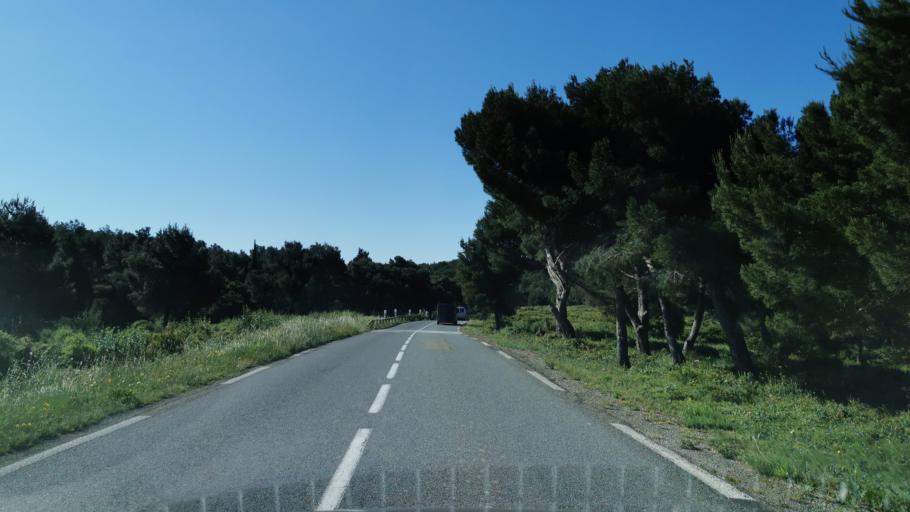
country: FR
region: Languedoc-Roussillon
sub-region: Departement de l'Aude
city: Armissan
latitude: 43.1585
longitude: 3.1511
